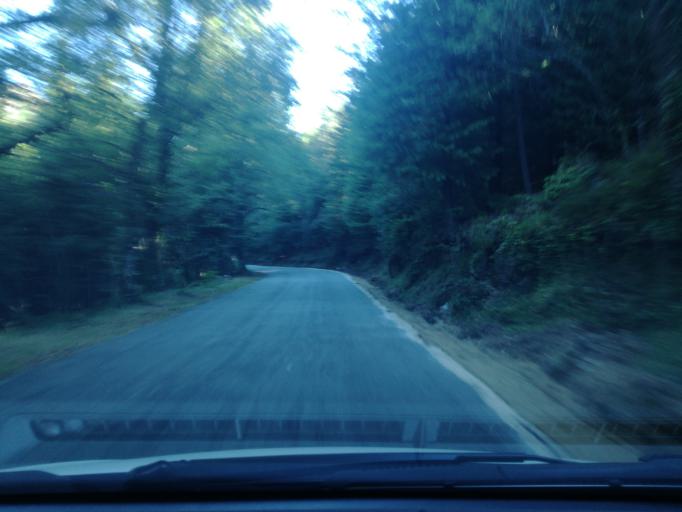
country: ES
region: Galicia
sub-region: Provincia de Ourense
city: Lobios
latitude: 41.7723
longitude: -8.1440
